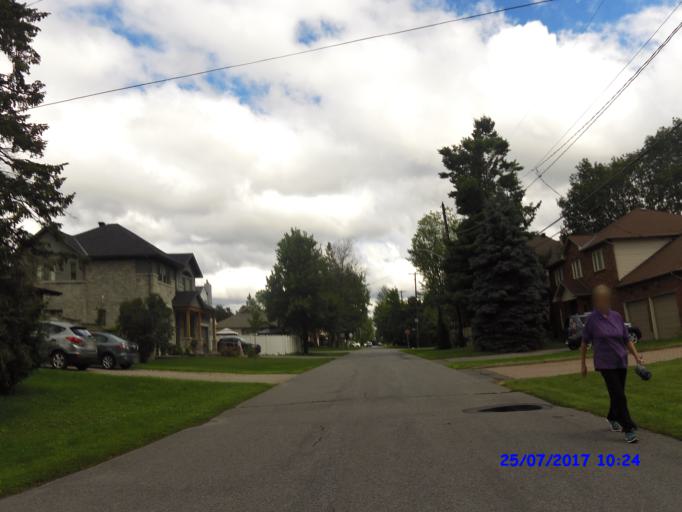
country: CA
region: Ontario
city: Ottawa
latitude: 45.3560
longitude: -75.7053
